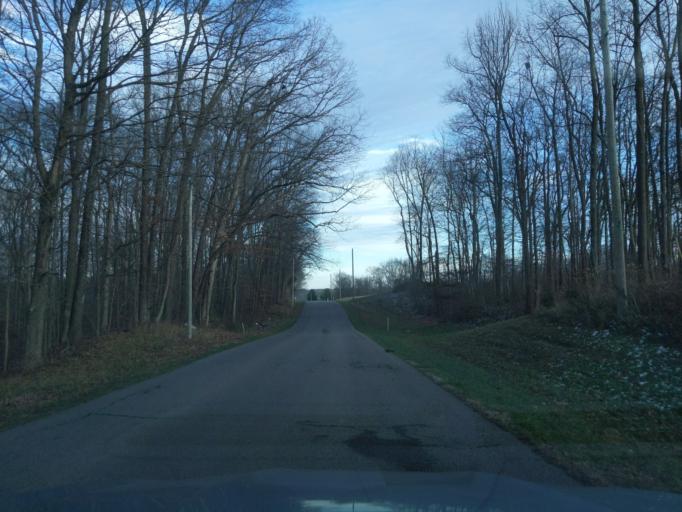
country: US
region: Indiana
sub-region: Decatur County
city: Westport
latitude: 39.2334
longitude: -85.5361
